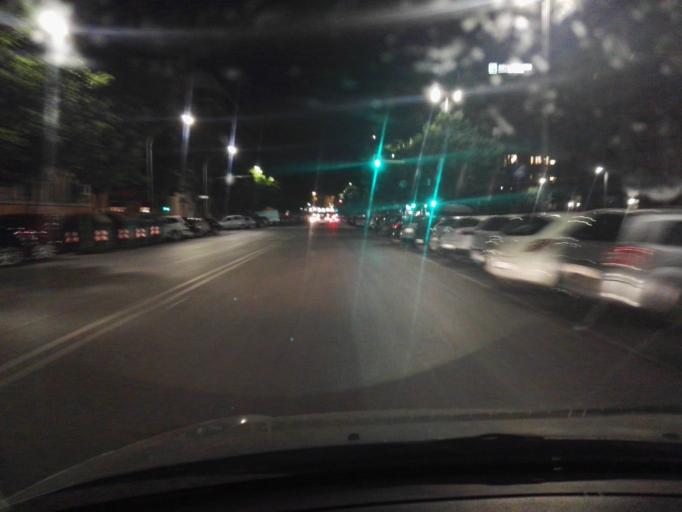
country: VA
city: Vatican City
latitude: 41.8762
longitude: 12.4678
